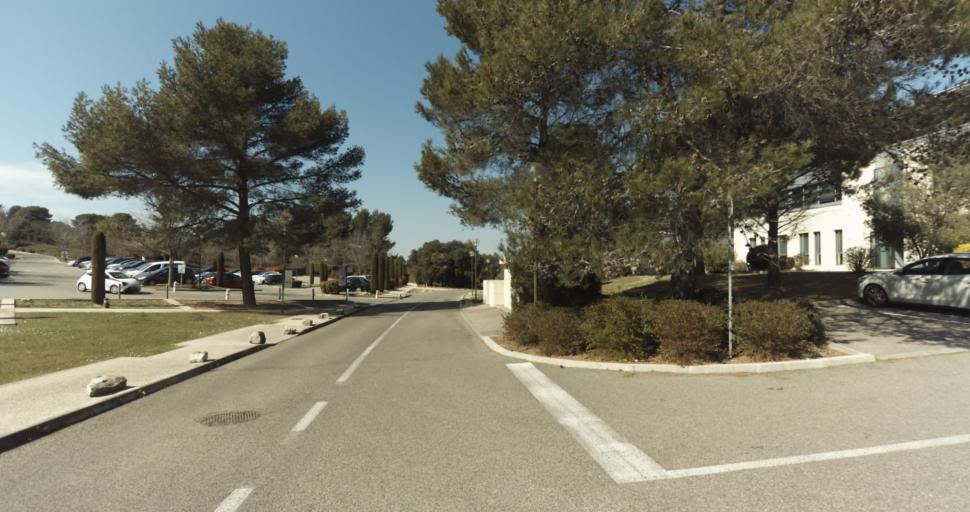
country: FR
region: Provence-Alpes-Cote d'Azur
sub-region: Departement des Bouches-du-Rhone
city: Cabries
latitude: 43.4743
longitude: 5.3686
